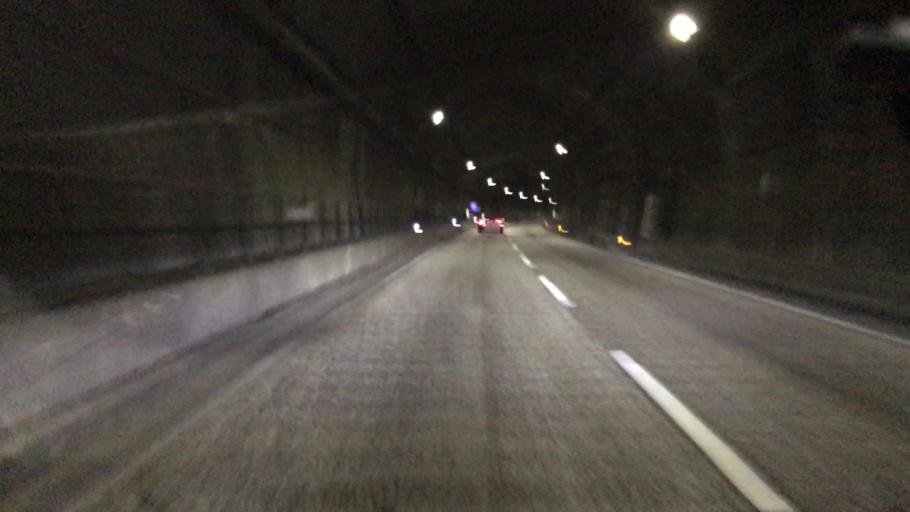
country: JP
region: Hyogo
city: Kobe
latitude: 34.7429
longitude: 135.1709
